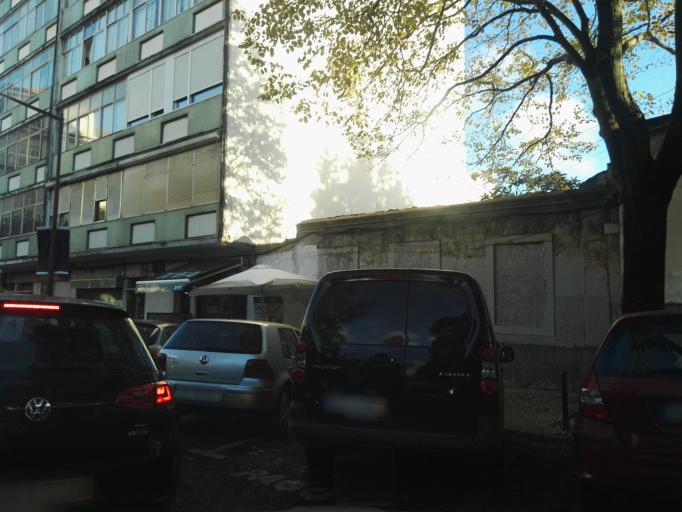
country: PT
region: Setubal
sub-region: Almada
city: Cacilhas
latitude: 38.7133
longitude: -9.1693
